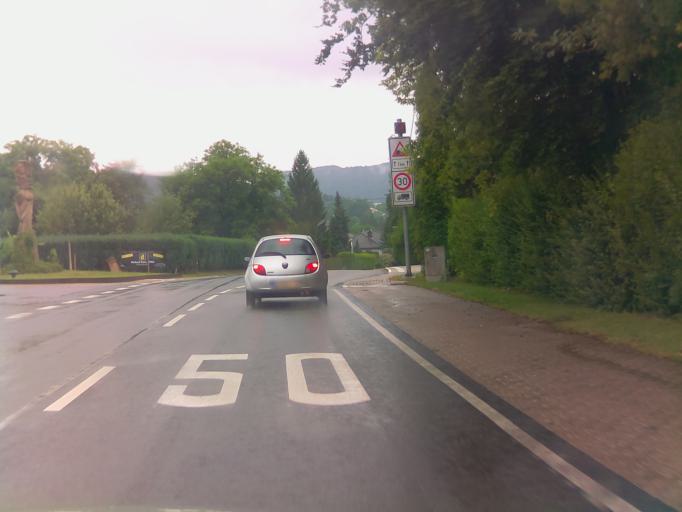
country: DE
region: Saarland
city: Perl
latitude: 49.4774
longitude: 6.3939
